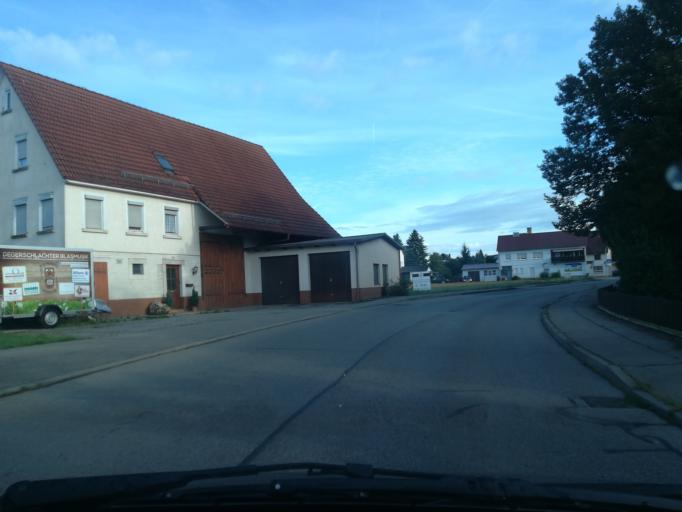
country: DE
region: Baden-Wuerttemberg
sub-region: Tuebingen Region
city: Sickenhausen
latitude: 48.5190
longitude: 9.1760
